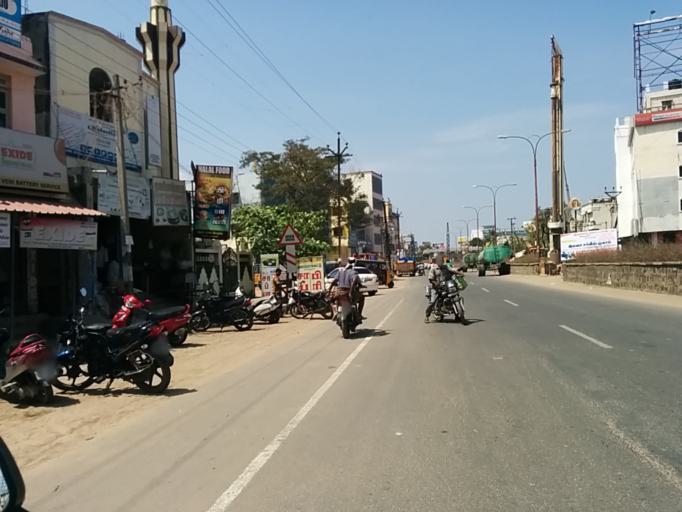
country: IN
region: Pondicherry
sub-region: Puducherry
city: Puducherry
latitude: 11.9228
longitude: 79.8087
